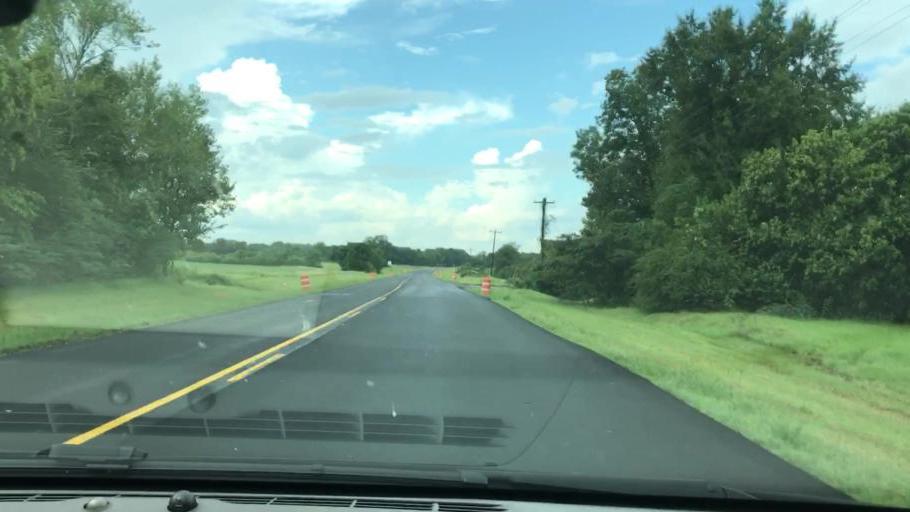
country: US
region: Georgia
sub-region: Early County
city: Blakely
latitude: 31.3955
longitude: -84.9506
